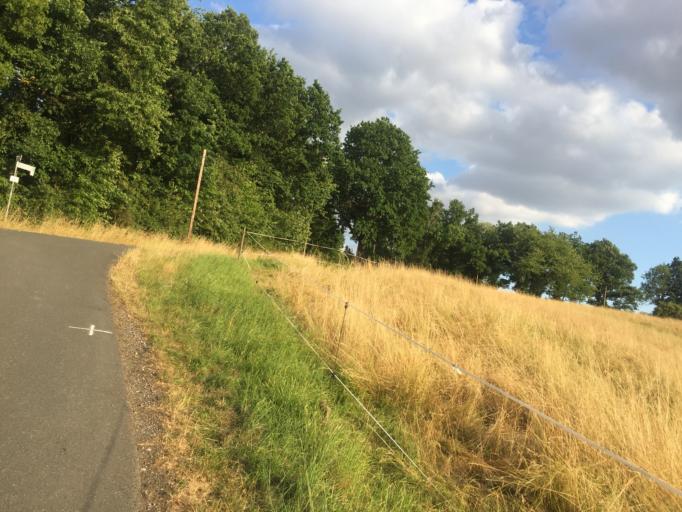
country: DE
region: Hesse
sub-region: Regierungsbezirk Giessen
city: Heuchelheim
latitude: 50.6127
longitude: 8.6022
